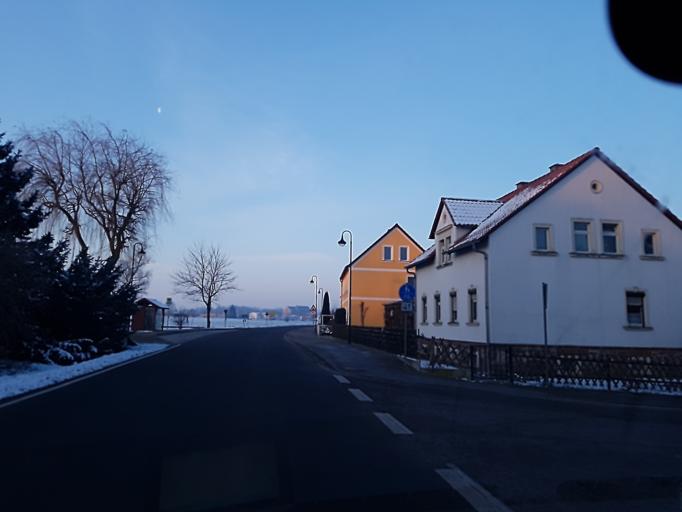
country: DE
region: Saxony
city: Mugeln
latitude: 51.2411
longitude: 13.0782
